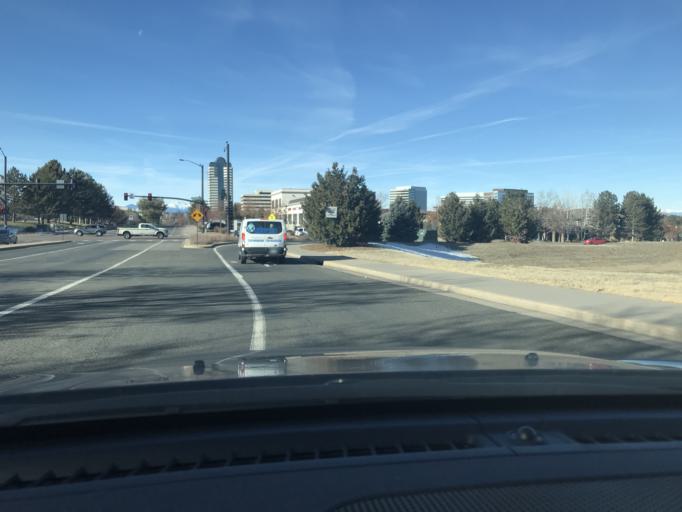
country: US
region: Colorado
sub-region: Arapahoe County
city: Centennial
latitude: 39.5987
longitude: -104.8799
